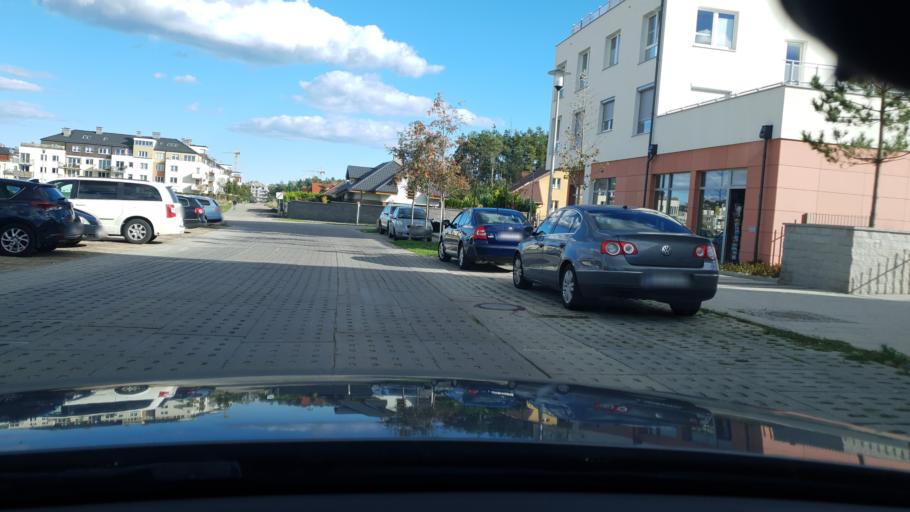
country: PL
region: Pomeranian Voivodeship
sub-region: Powiat kartuski
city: Chwaszczyno
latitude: 54.4928
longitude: 18.4355
